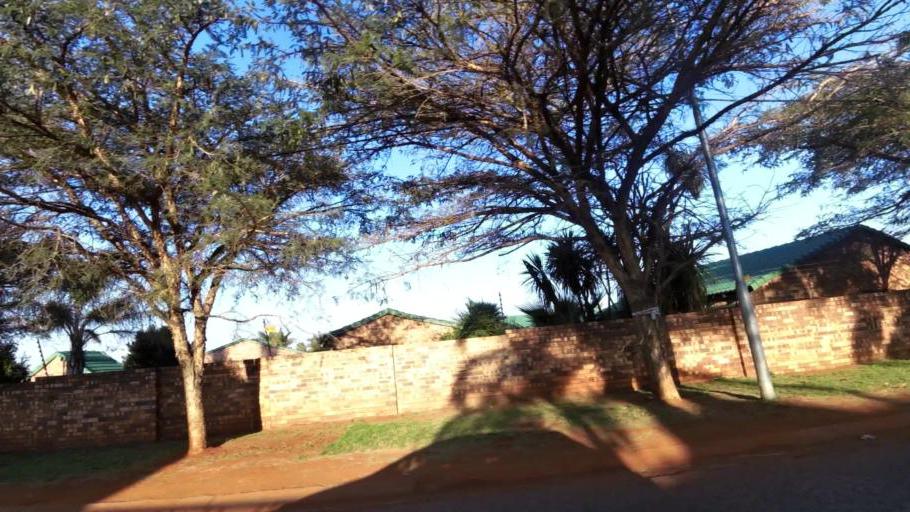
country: ZA
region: Gauteng
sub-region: City of Johannesburg Metropolitan Municipality
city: Roodepoort
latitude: -26.1680
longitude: 27.9465
